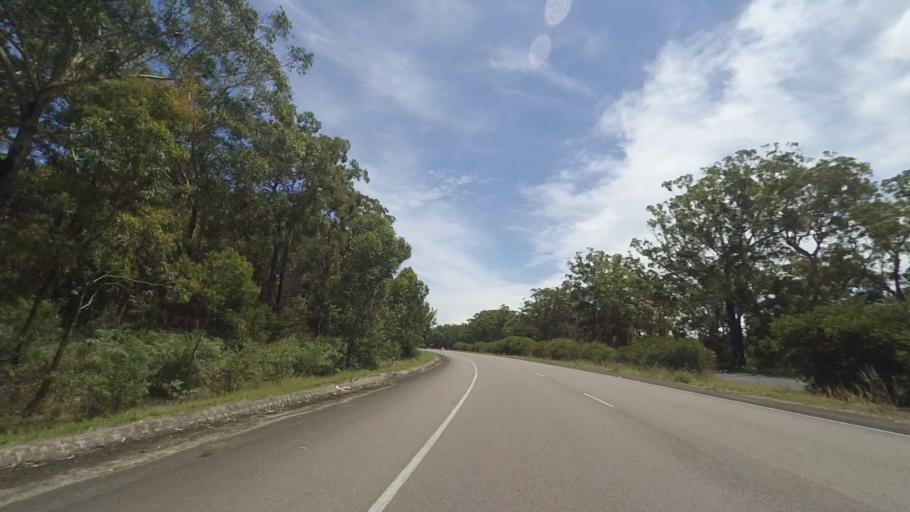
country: AU
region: New South Wales
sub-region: Port Stephens Shire
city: Anna Bay
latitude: -32.7736
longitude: 152.0073
